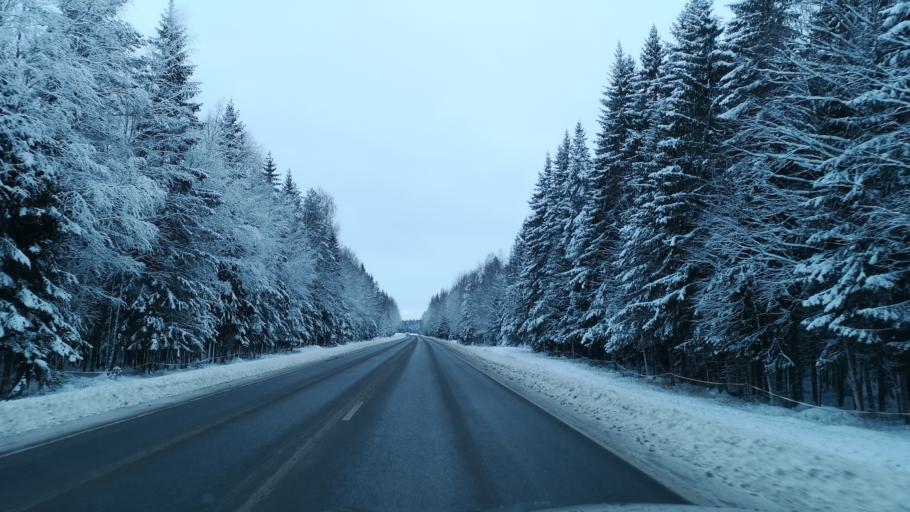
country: FI
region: Varsinais-Suomi
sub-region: Loimaa
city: Loimaa
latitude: 60.9116
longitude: 23.1732
